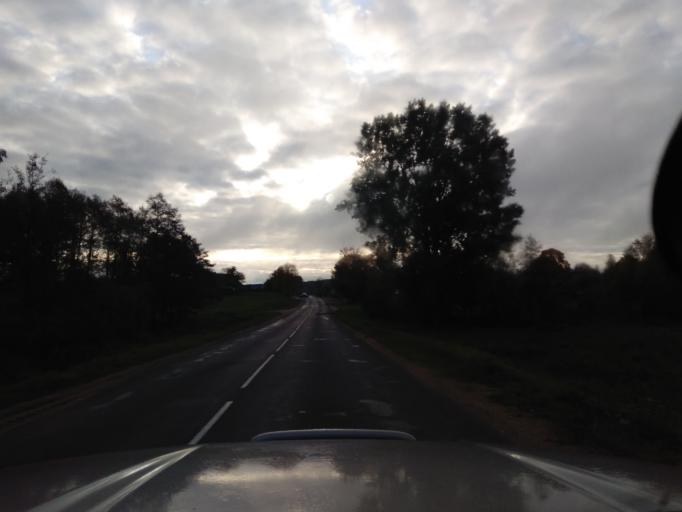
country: BY
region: Minsk
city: Kapyl'
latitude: 53.1604
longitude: 27.0900
